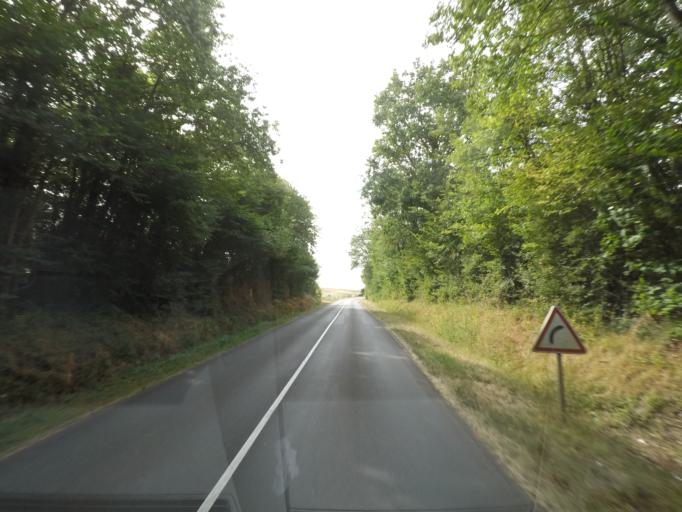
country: FR
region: Poitou-Charentes
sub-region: Departement de la Charente
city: Nanteuil-en-Vallee
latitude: 45.9862
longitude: 0.3465
